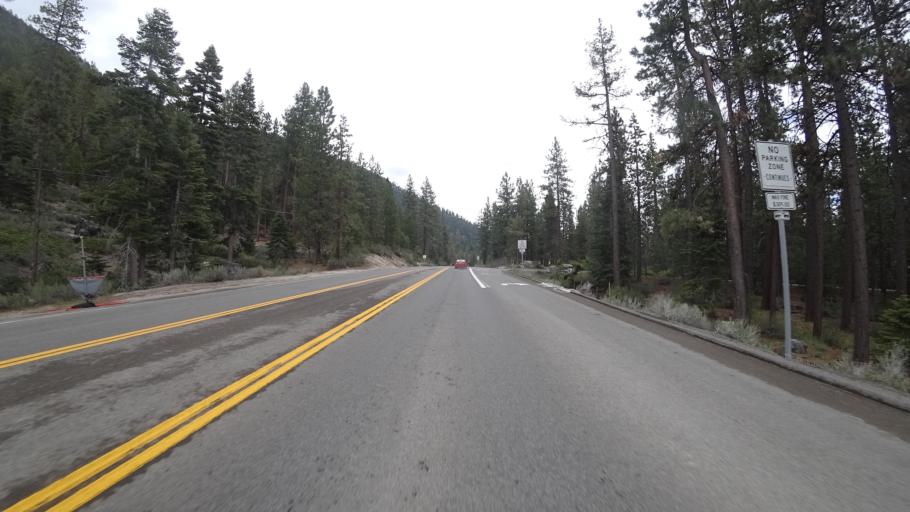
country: US
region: Nevada
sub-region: Washoe County
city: Incline Village
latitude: 39.1994
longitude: -119.9284
